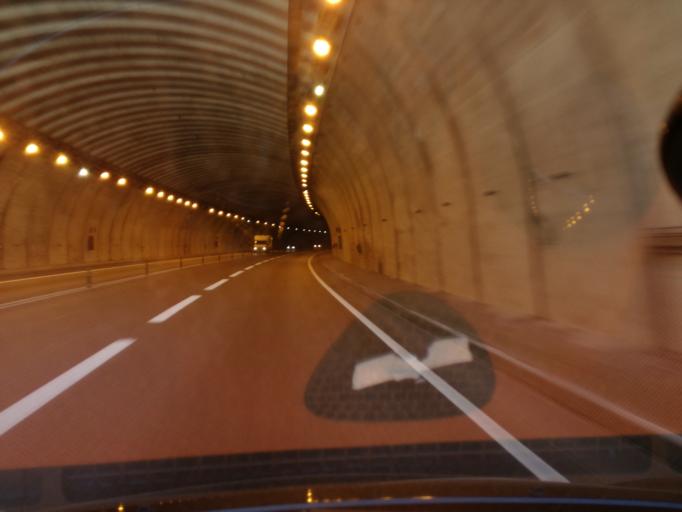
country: PT
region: Viana do Castelo
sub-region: Vila Nova de Cerveira
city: Vila Nova de Cerveira
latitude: 41.9095
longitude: -8.7835
